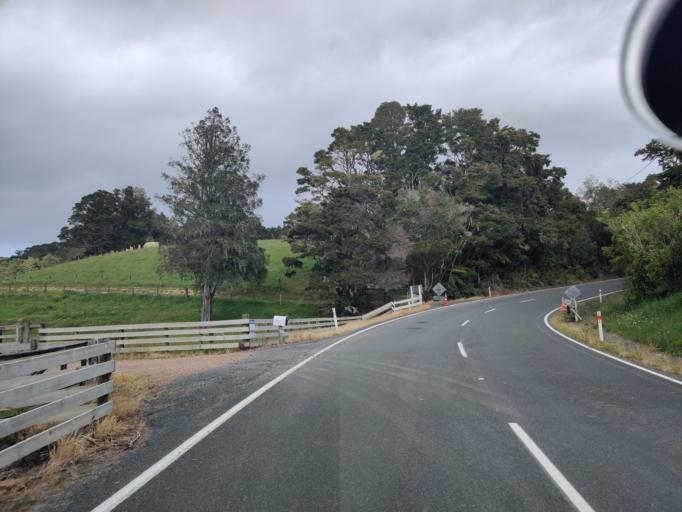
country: NZ
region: Northland
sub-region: Whangarei
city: Ngunguru
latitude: -35.5774
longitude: 174.3987
